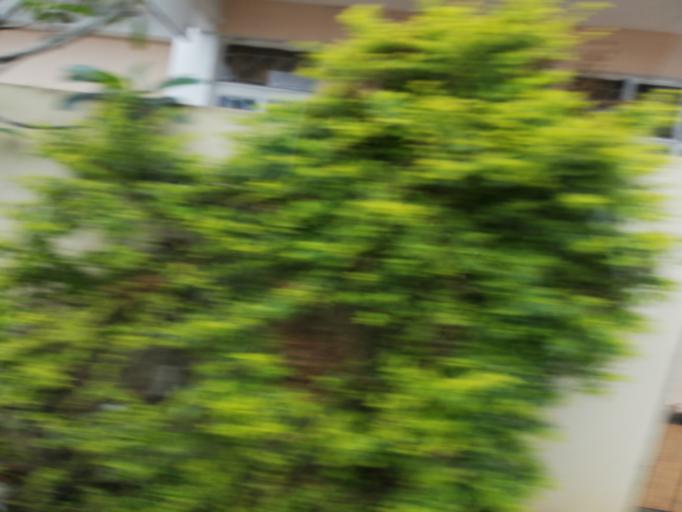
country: MU
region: Black River
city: Gros Cailloux
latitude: -20.2324
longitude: 57.4536
